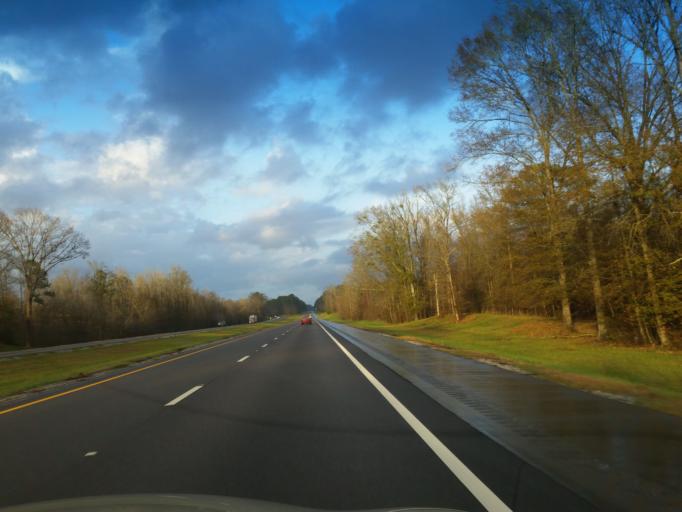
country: US
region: Mississippi
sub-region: Jones County
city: Sharon
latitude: 31.9385
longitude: -88.9908
